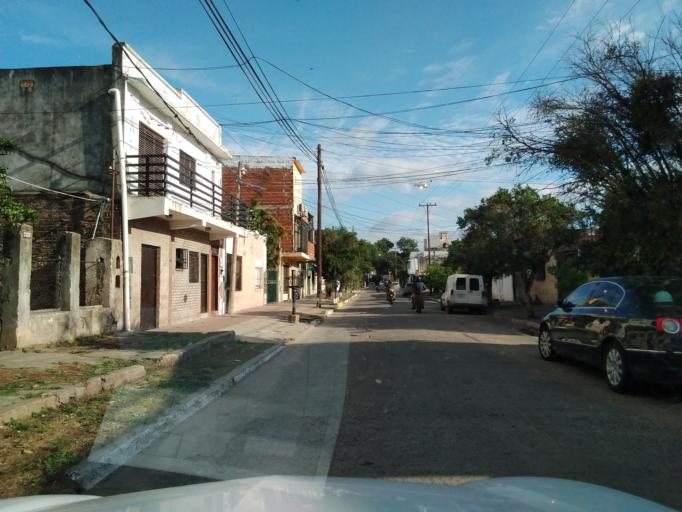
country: AR
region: Corrientes
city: Corrientes
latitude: -27.4649
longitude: -58.8193
